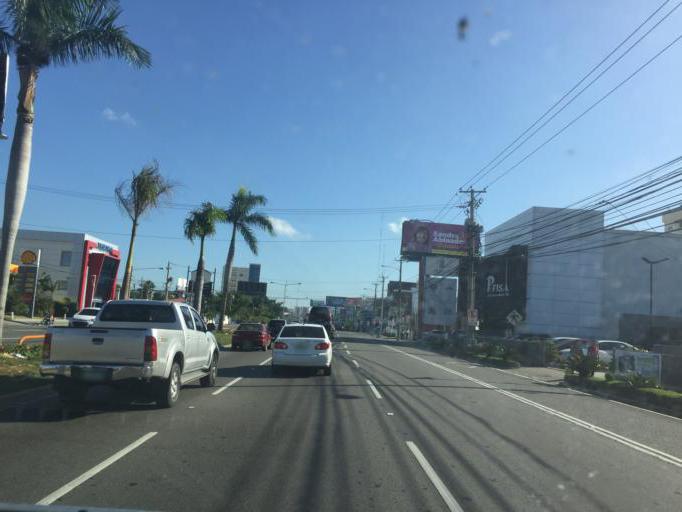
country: DO
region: Nacional
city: Bella Vista
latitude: 18.4534
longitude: -69.9573
